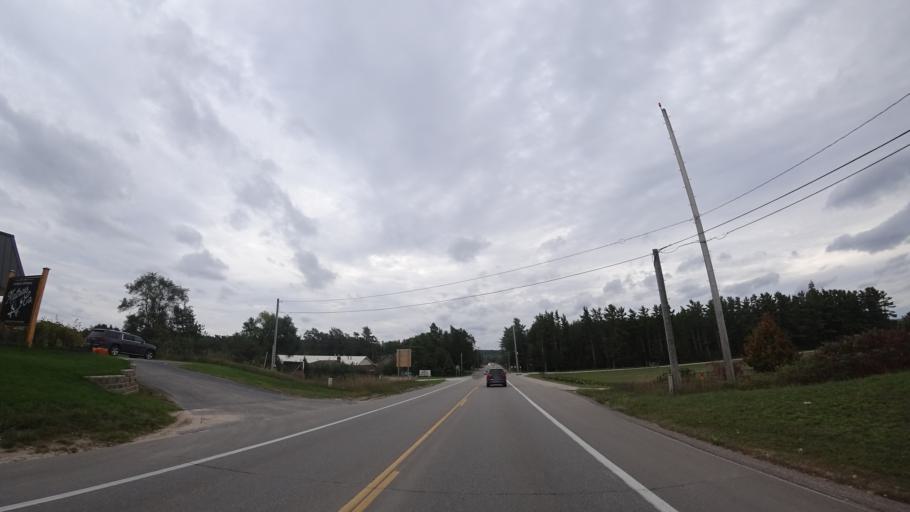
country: US
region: Michigan
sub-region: Emmet County
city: Petoskey
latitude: 45.4257
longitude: -84.9045
